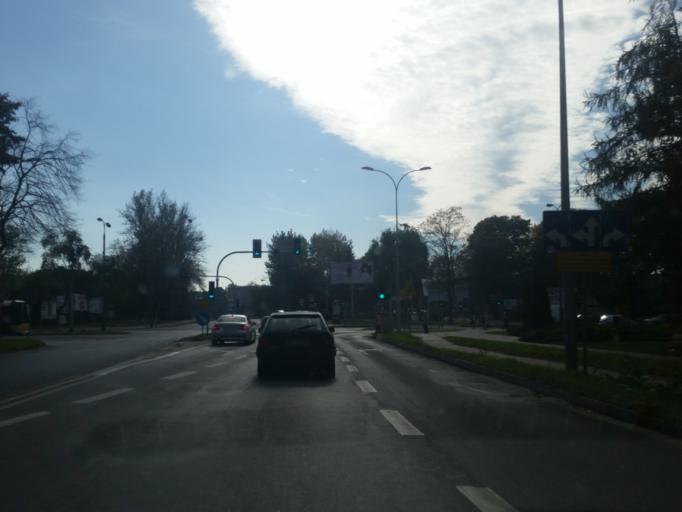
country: PL
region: Masovian Voivodeship
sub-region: Plock
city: Plock
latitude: 52.5515
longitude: 19.6827
